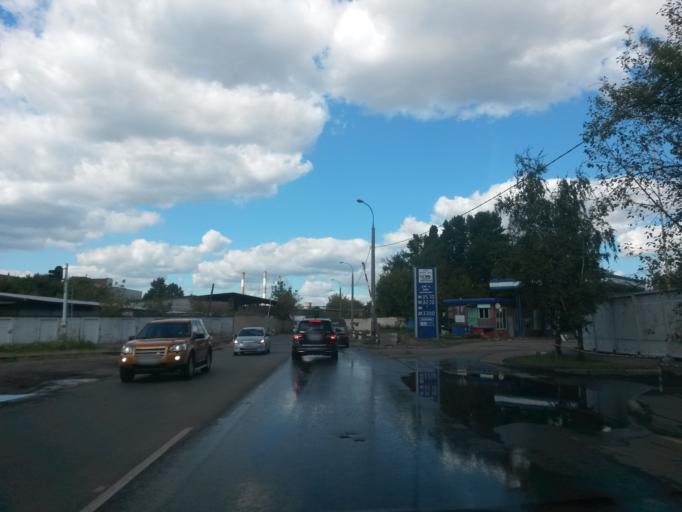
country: RU
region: Moskovskaya
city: Kozhukhovo
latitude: 55.7059
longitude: 37.7025
